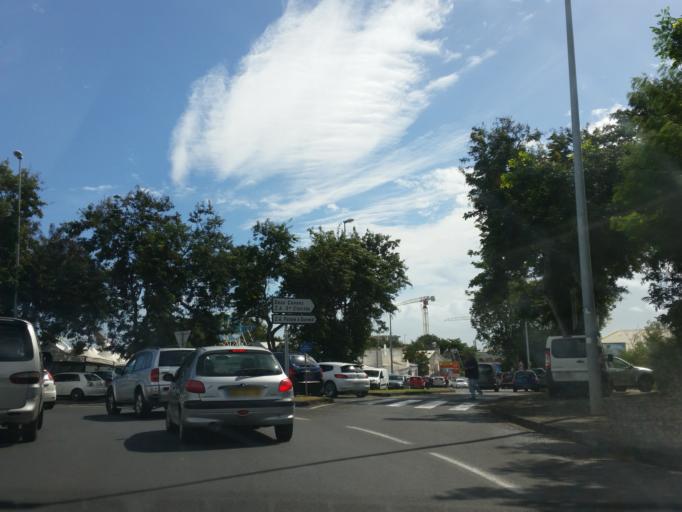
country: RE
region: Reunion
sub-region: Reunion
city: Saint-Denis
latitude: -20.8973
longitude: 55.4756
